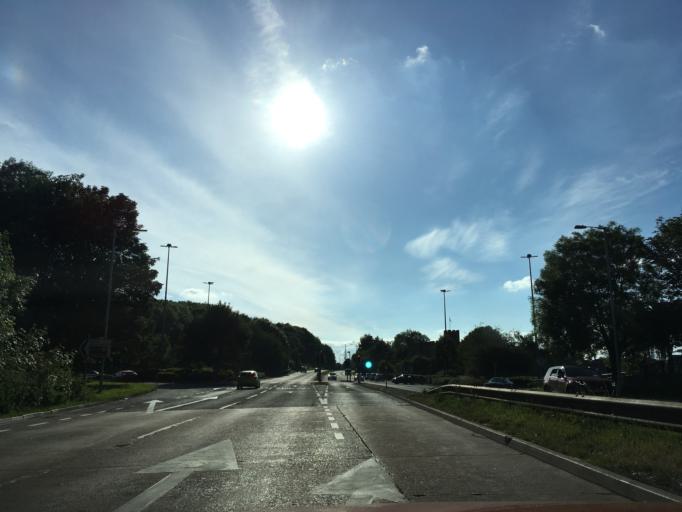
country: GB
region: England
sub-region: Somerset
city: Creech Saint Michael
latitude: 51.0242
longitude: -3.0700
